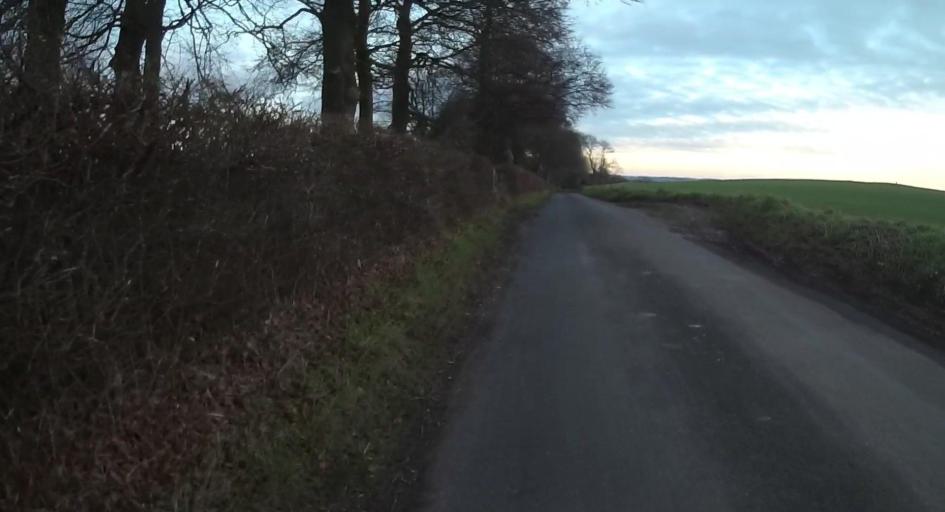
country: GB
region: England
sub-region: Hampshire
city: Swanmore
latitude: 51.0127
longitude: -1.1452
